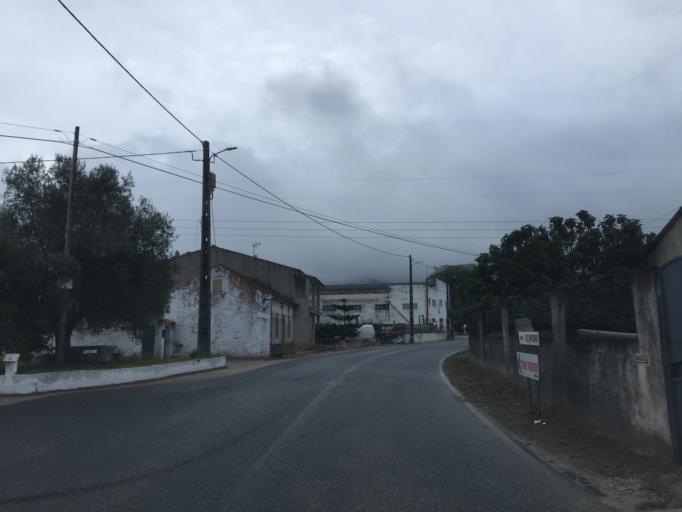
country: PT
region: Leiria
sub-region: Alcobaca
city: Benedita
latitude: 39.4325
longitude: -8.9536
